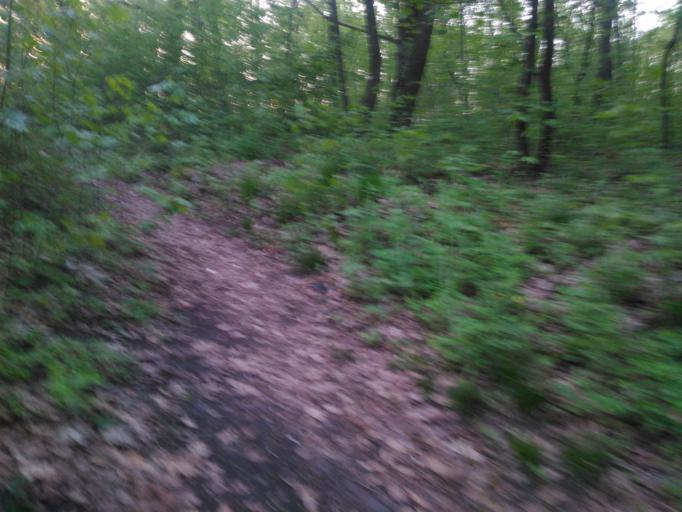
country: RU
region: Ulyanovsk
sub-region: Ulyanovskiy Rayon
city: Ulyanovsk
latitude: 54.2726
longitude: 48.3378
